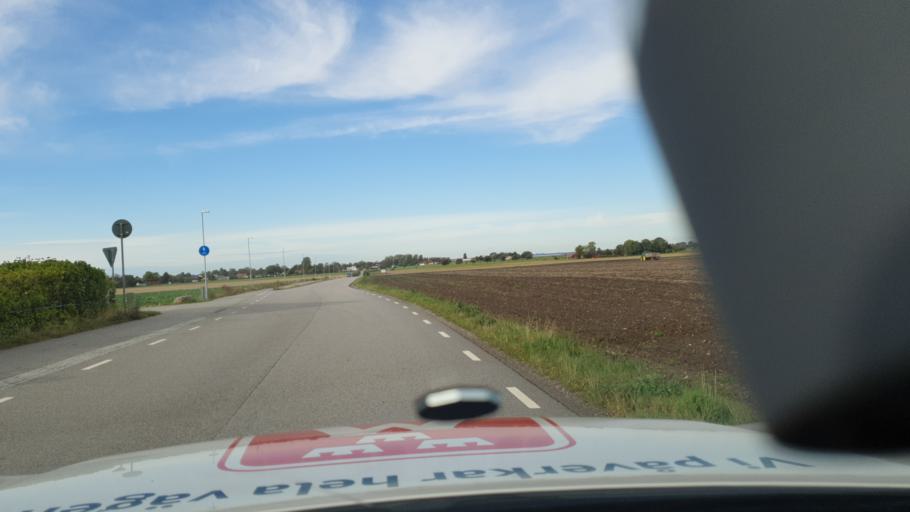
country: SE
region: Skane
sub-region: Malmo
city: Tygelsjo
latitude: 55.5001
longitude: 12.9759
